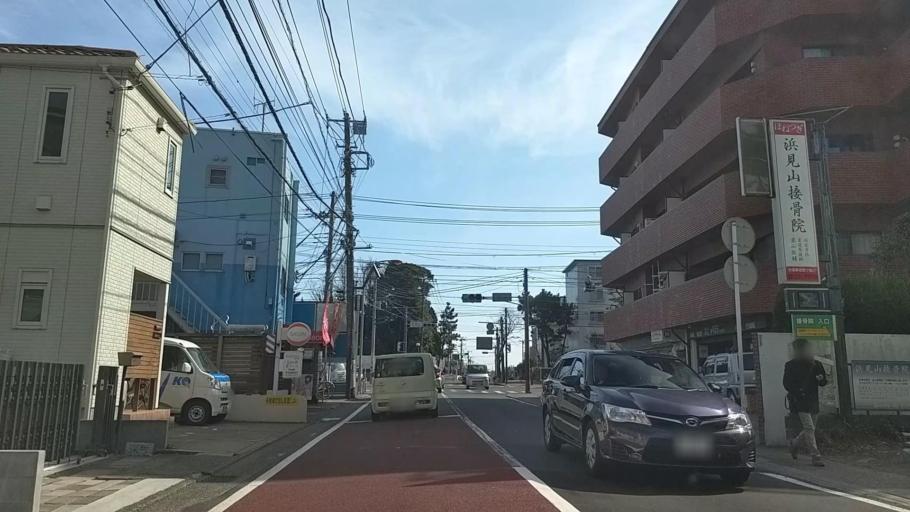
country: JP
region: Kanagawa
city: Fujisawa
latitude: 35.3276
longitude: 139.4528
